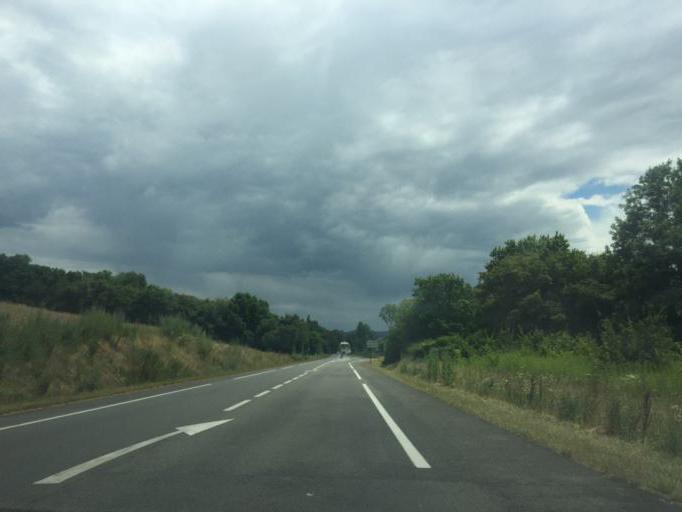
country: FR
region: Rhone-Alpes
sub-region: Departement de l'Isere
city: Charvieu-Chavagneux
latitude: 45.7566
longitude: 5.1325
